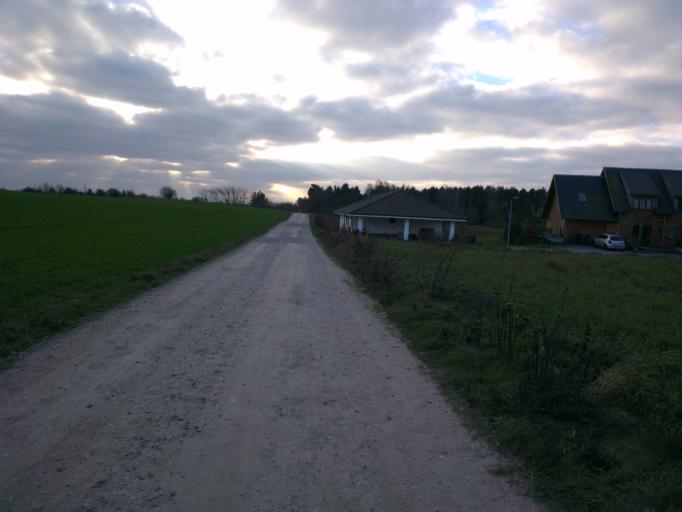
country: DK
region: Capital Region
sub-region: Frederikssund Kommune
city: Jaegerspris
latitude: 55.8465
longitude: 11.9979
